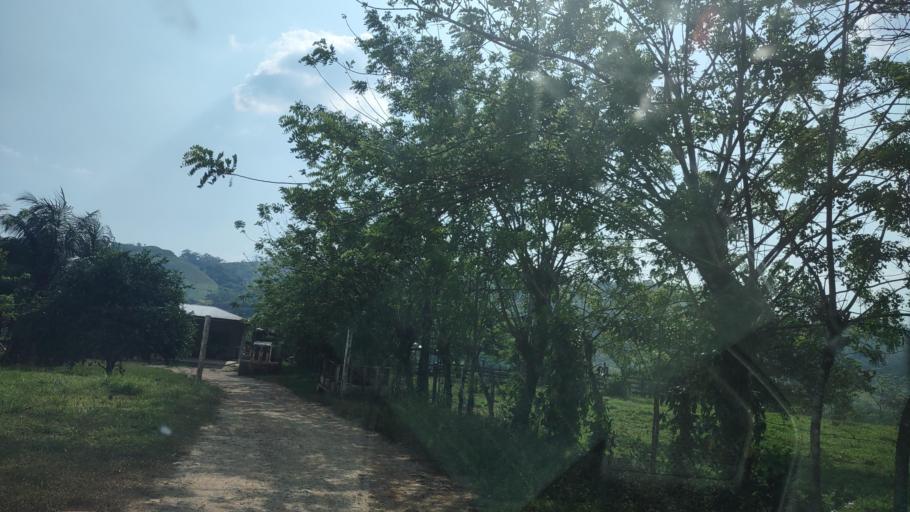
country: MX
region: Chiapas
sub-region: Tecpatan
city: Raudales Malpaso
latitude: 17.3370
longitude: -93.7530
